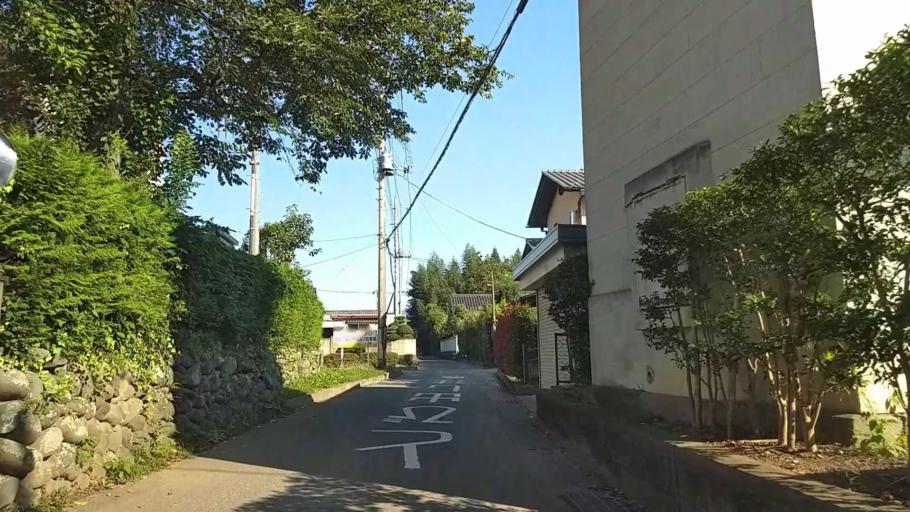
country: JP
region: Gunma
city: Annaka
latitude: 36.3300
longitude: 138.8980
